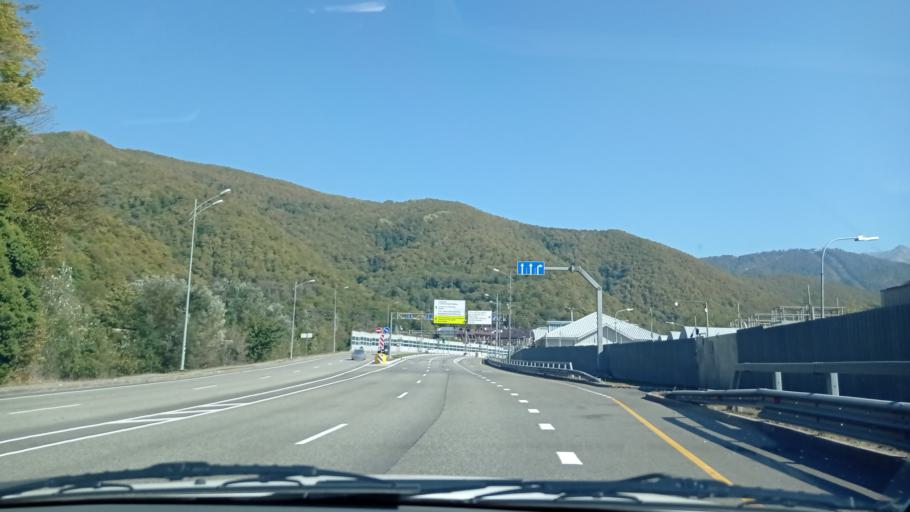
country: RU
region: Krasnodarskiy
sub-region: Sochi City
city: Krasnaya Polyana
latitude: 43.6856
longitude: 40.2432
